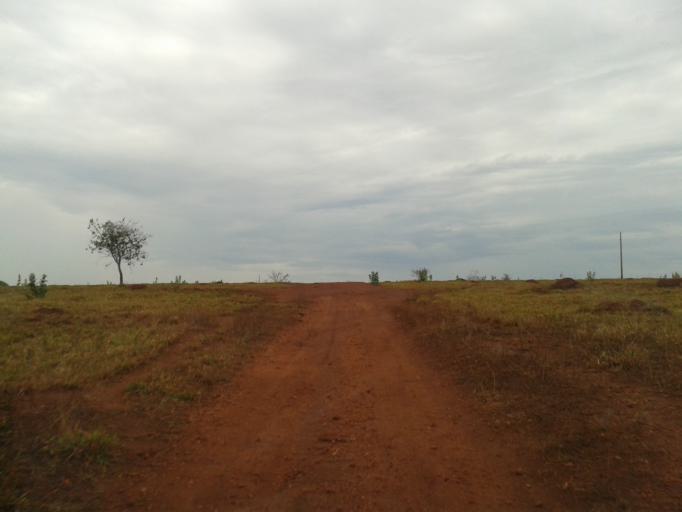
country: BR
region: Minas Gerais
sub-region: Santa Vitoria
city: Santa Vitoria
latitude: -18.8656
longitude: -49.8249
